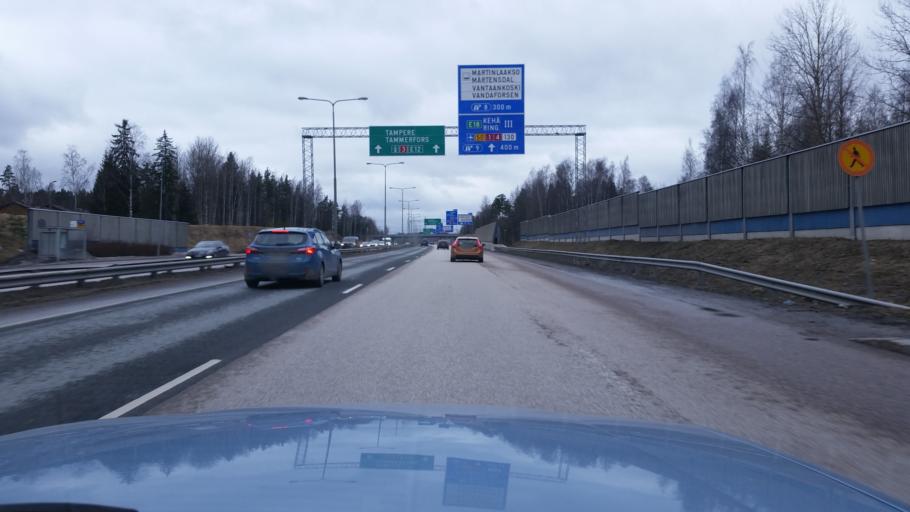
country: FI
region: Uusimaa
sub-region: Helsinki
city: Teekkarikylae
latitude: 60.2834
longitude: 24.8656
